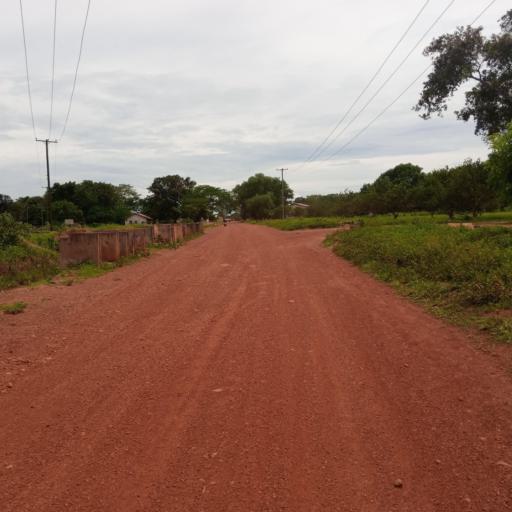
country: SL
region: Southern Province
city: Largo
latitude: 8.1121
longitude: -12.0752
